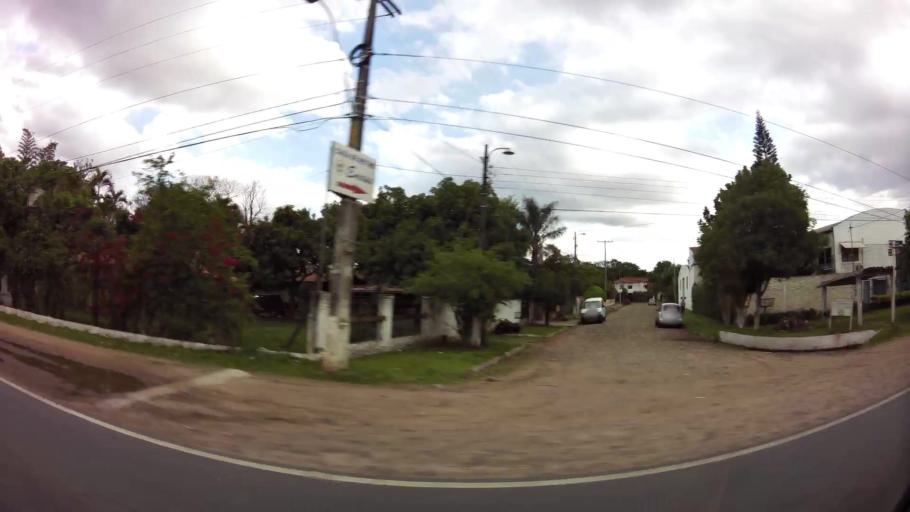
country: PY
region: Central
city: Fernando de la Mora
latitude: -25.2800
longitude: -57.5299
